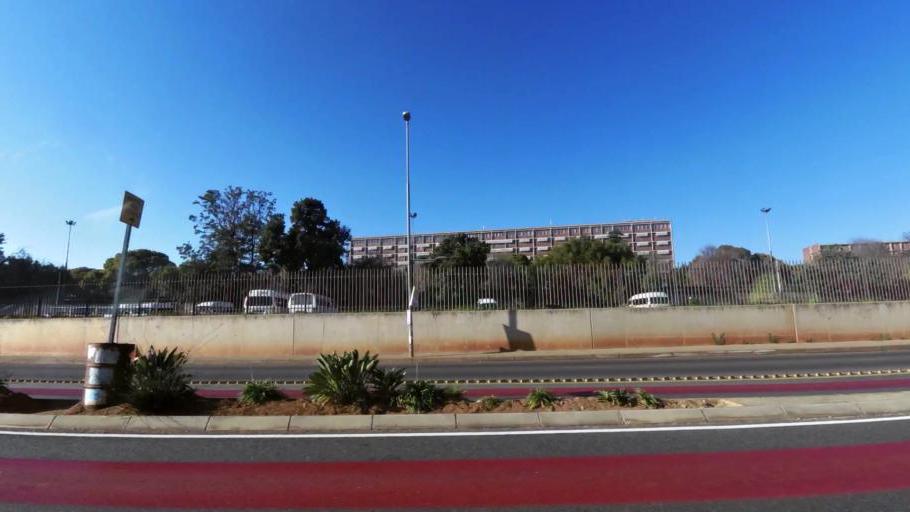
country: ZA
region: Gauteng
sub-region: City of Johannesburg Metropolitan Municipality
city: Johannesburg
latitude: -26.1837
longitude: 27.9893
